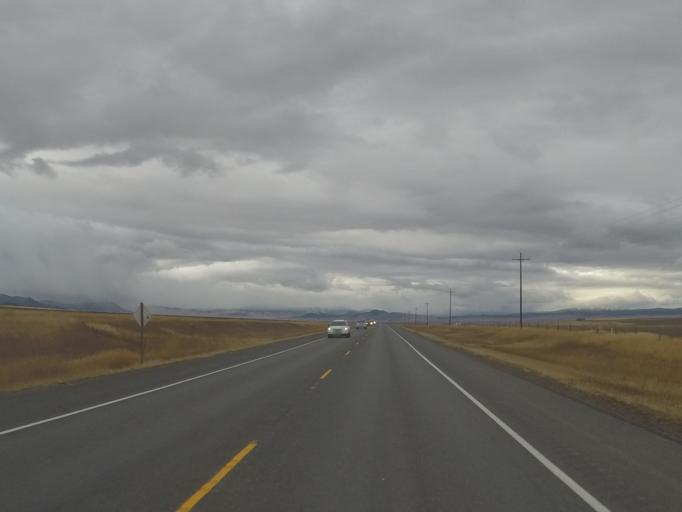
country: US
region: Montana
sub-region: Lewis and Clark County
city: East Helena
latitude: 46.5740
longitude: -111.8306
